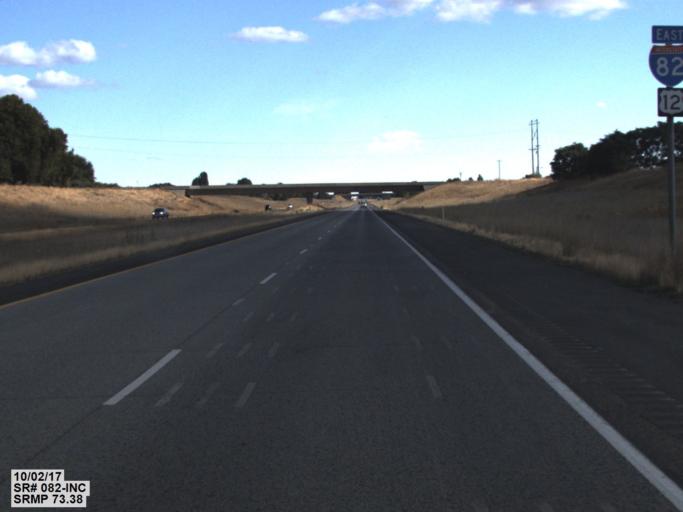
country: US
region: Washington
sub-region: Yakima County
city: Grandview
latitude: 46.2672
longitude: -119.9088
